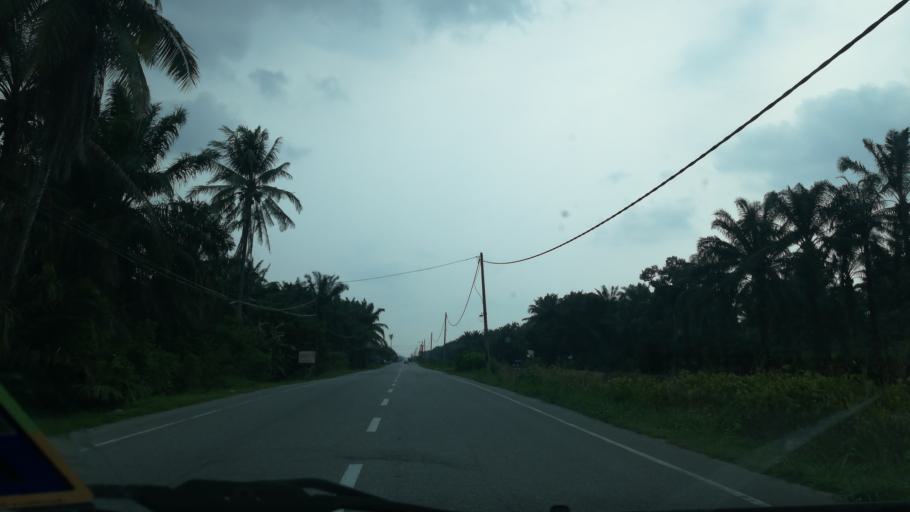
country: MY
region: Perak
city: Teluk Intan
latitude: 4.1145
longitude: 101.0707
